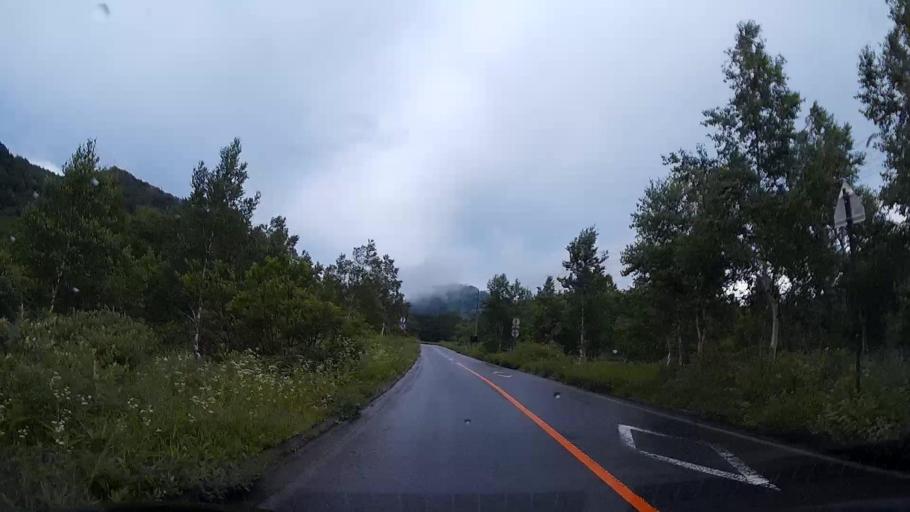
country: JP
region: Nagano
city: Nakano
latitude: 36.6921
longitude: 138.4922
